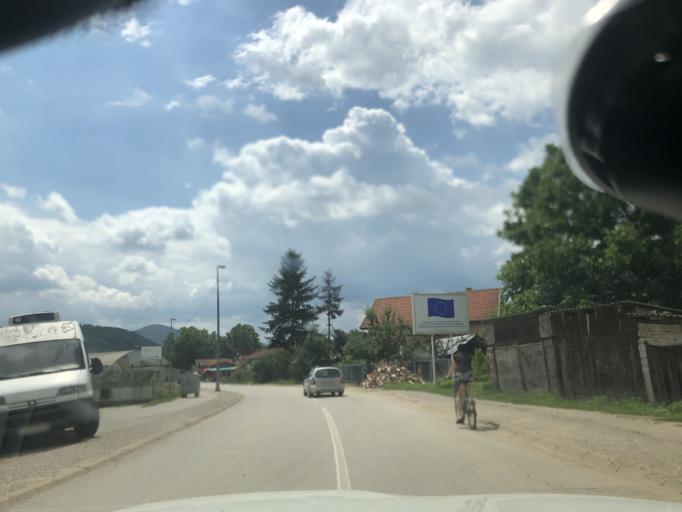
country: RS
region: Central Serbia
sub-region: Jablanicki Okrug
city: Medvega
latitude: 42.8453
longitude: 21.5869
